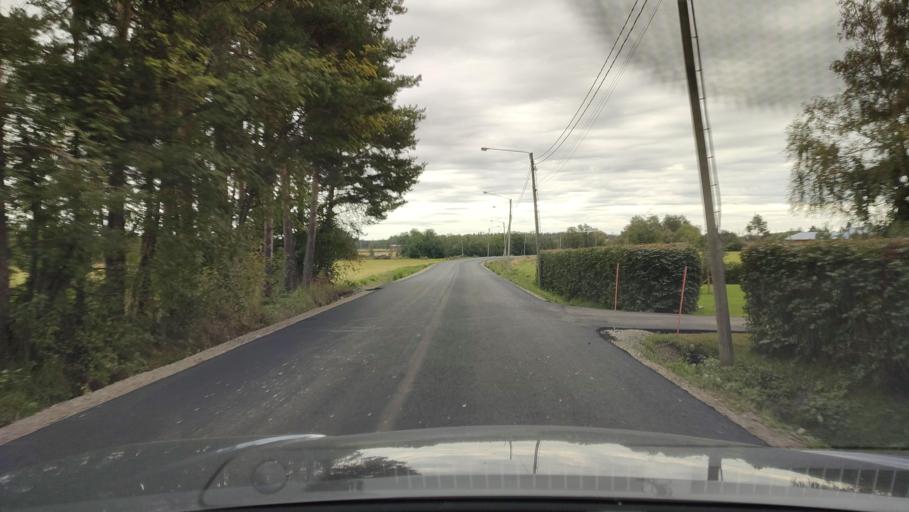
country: FI
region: Southern Ostrobothnia
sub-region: Suupohja
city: Karijoki
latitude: 62.2494
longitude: 21.5497
